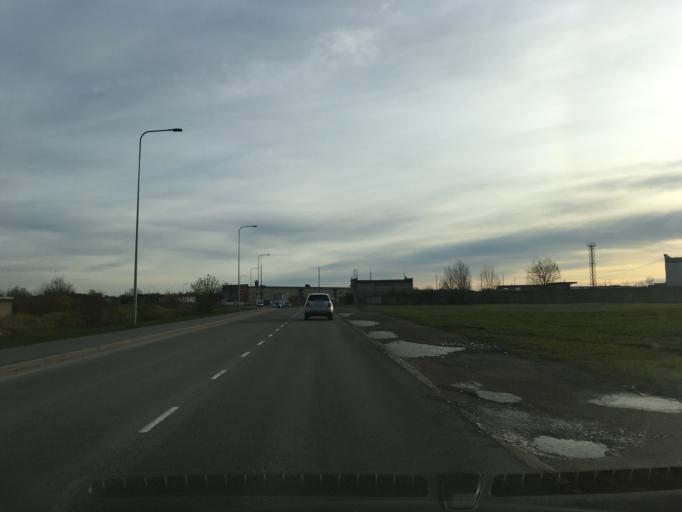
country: EE
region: Ida-Virumaa
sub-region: Narva linn
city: Narva
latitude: 59.3643
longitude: 28.1714
